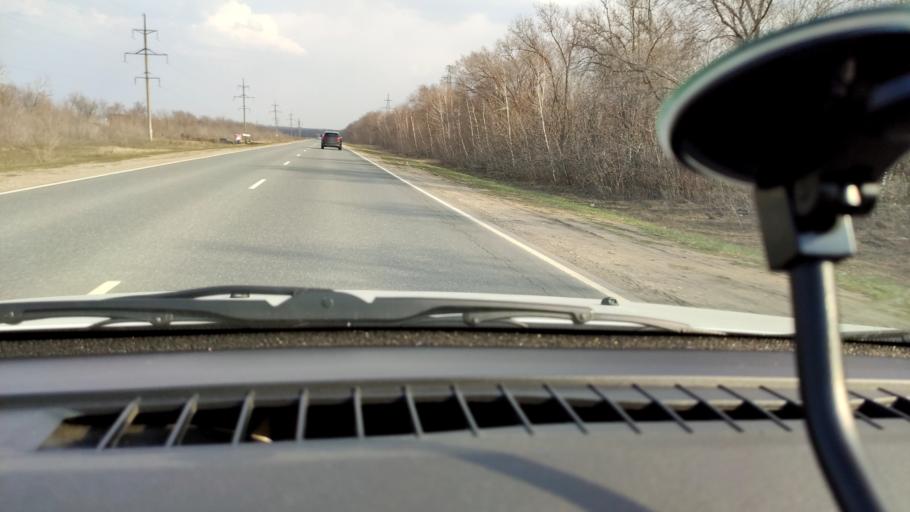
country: RU
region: Samara
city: Dubovyy Umet
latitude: 53.0977
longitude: 50.2666
